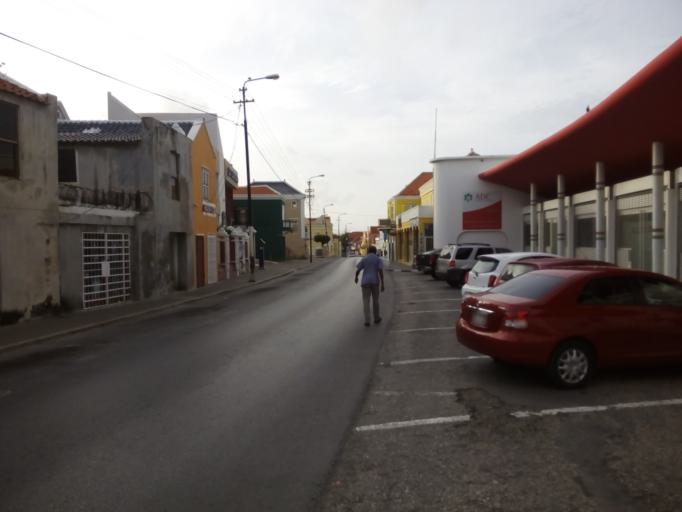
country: CW
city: Willemstad
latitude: 12.1113
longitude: -68.9407
